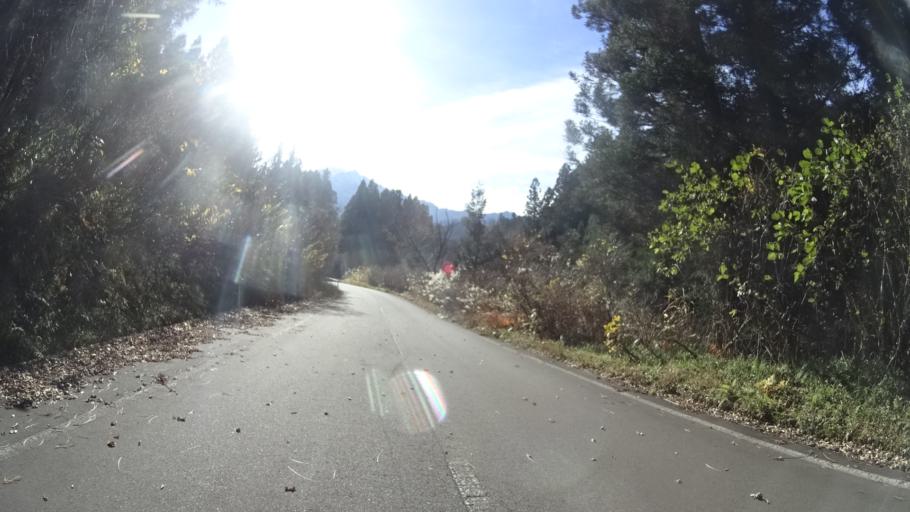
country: JP
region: Niigata
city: Muikamachi
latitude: 37.1758
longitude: 139.0866
